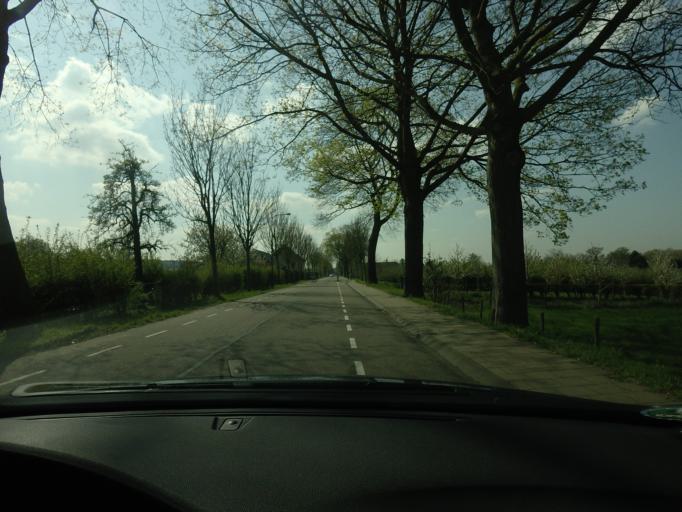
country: NL
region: Limburg
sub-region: Eijsden-Margraten
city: Eijsden
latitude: 50.8034
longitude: 5.7330
